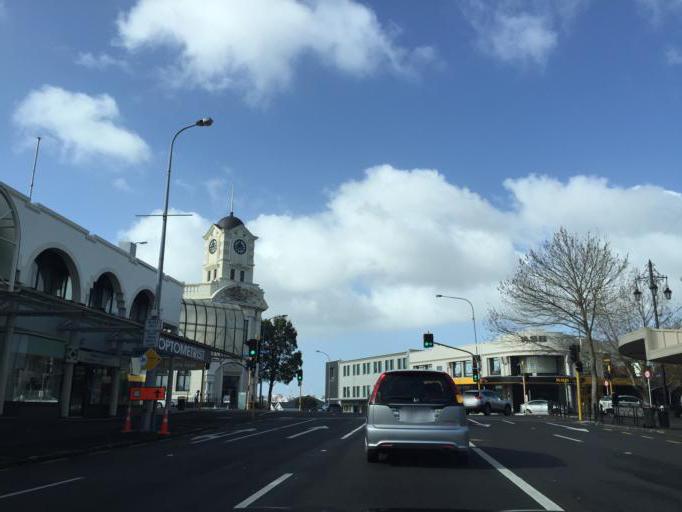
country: NZ
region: Auckland
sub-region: Auckland
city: Auckland
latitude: -36.8471
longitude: 174.7438
